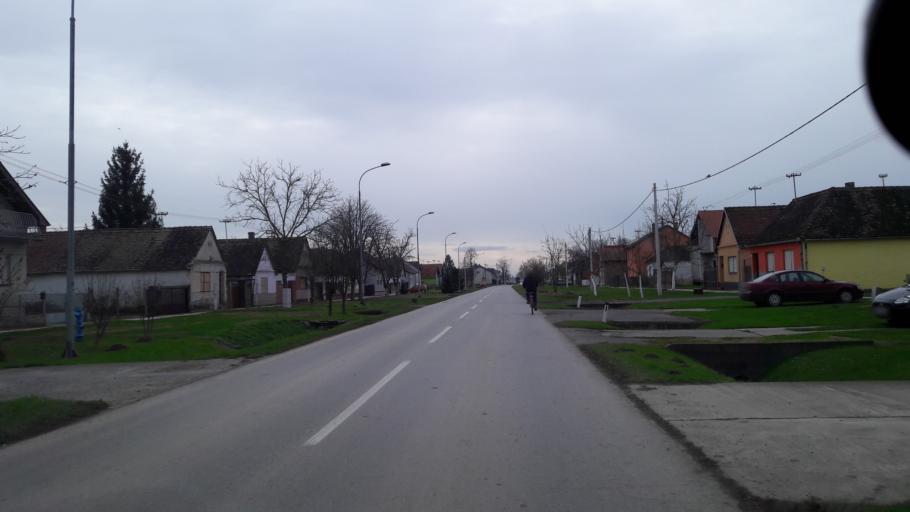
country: HR
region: Osjecko-Baranjska
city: Vladislavci
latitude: 45.4599
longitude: 18.5734
